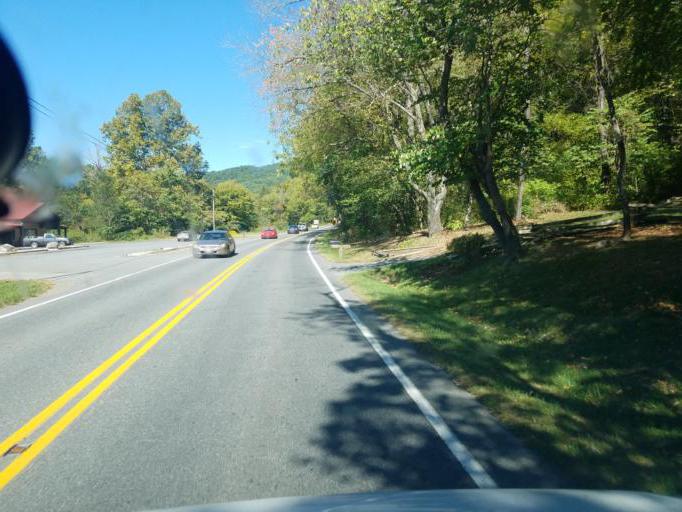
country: US
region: Virginia
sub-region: Greene County
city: Stanardsville
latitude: 38.3375
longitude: -78.5049
